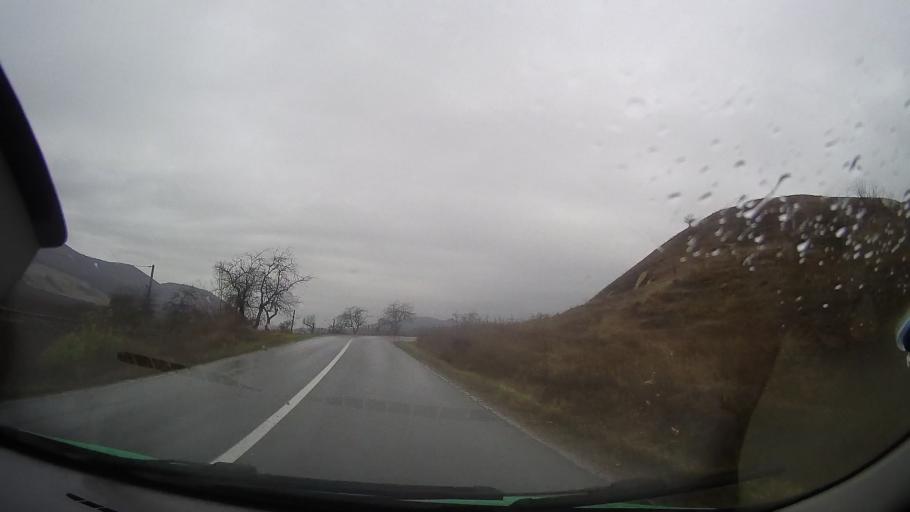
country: RO
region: Bistrita-Nasaud
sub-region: Comuna Mariselu
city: Mariselu
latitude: 47.0437
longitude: 24.4671
